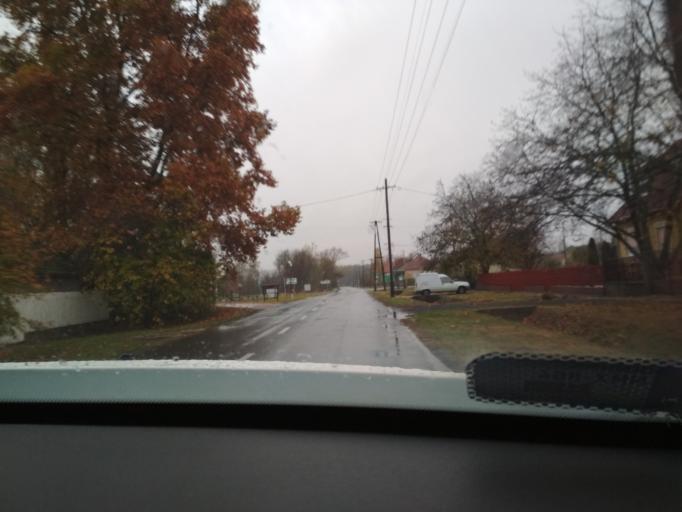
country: HU
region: Csongrad
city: Baks
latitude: 46.5410
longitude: 20.1018
